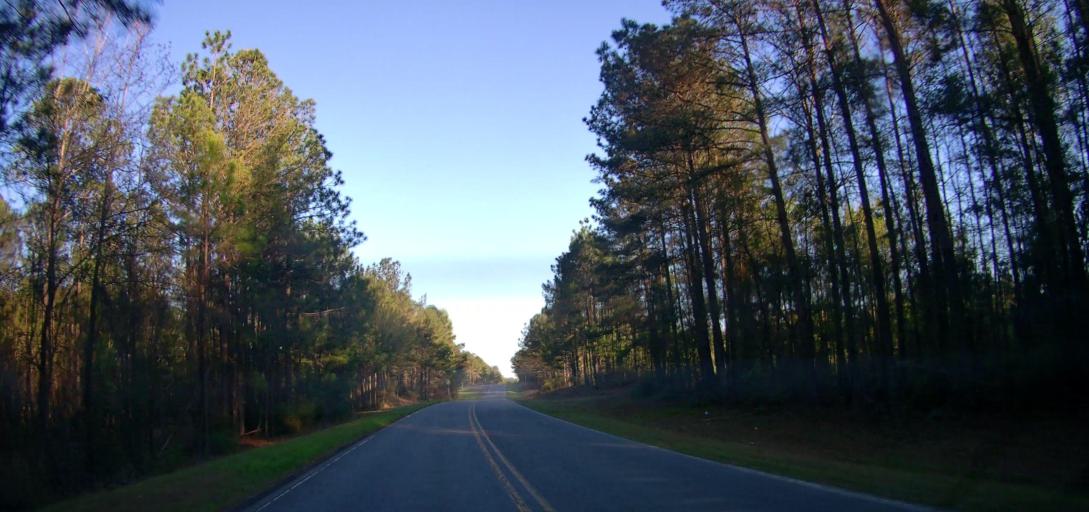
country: US
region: Georgia
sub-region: Wilkinson County
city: Gordon
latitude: 32.8763
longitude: -83.2510
